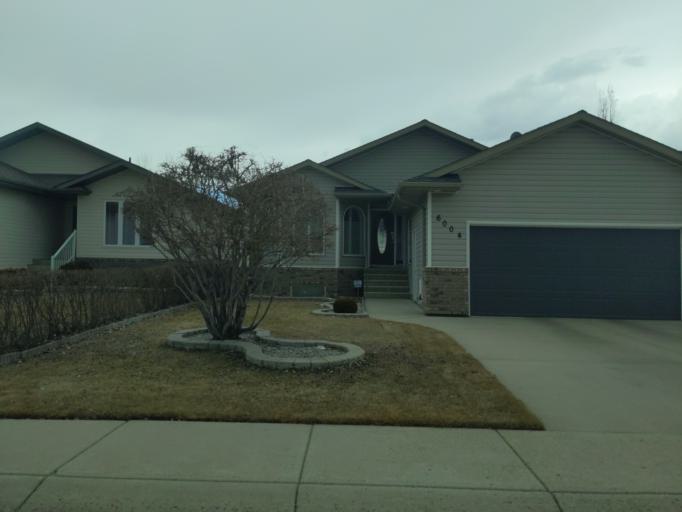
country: CA
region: Saskatchewan
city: Lloydminster
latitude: 53.2576
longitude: -110.0357
